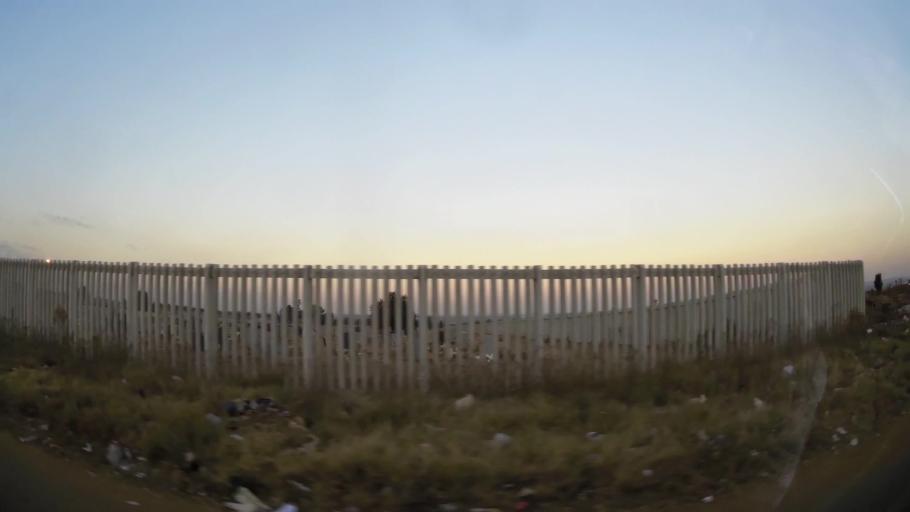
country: ZA
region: Gauteng
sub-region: West Rand District Municipality
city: Randfontein
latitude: -26.2128
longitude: 27.7139
